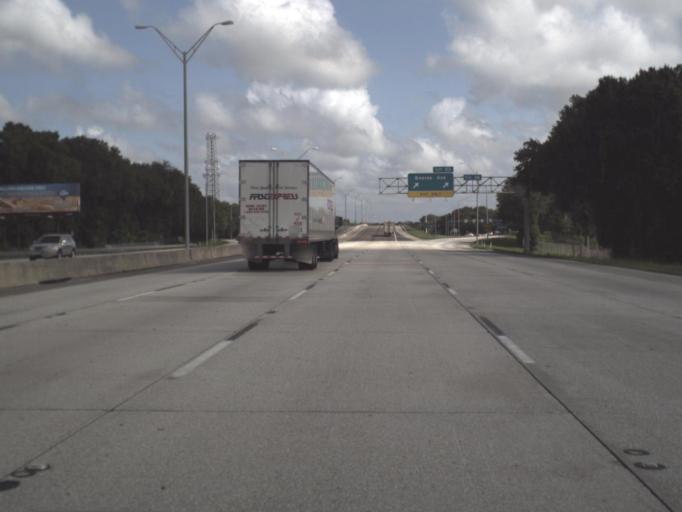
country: US
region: Florida
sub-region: Hillsborough County
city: Lake Magdalene
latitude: 28.0833
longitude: -82.4547
